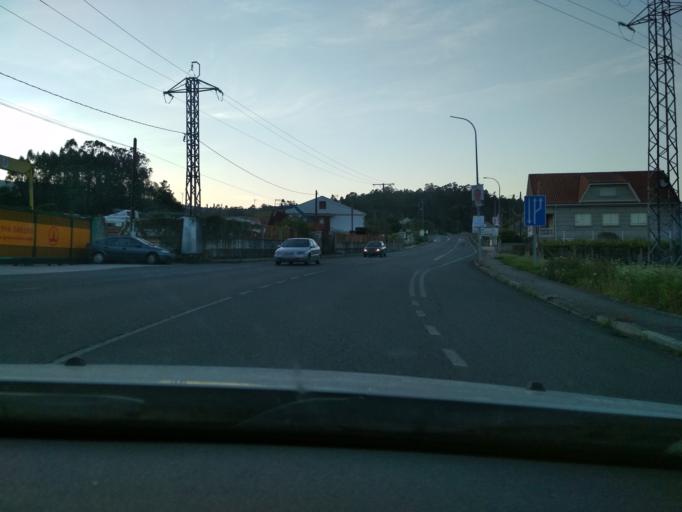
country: ES
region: Galicia
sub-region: Provincia de Pontevedra
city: Caldas de Reis
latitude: 42.6113
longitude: -8.6466
